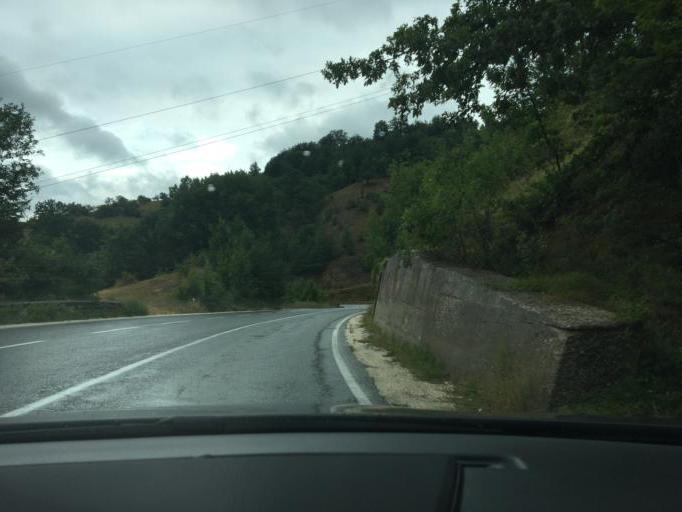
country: MK
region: Kriva Palanka
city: Kriva Palanka
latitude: 42.2196
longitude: 22.4337
